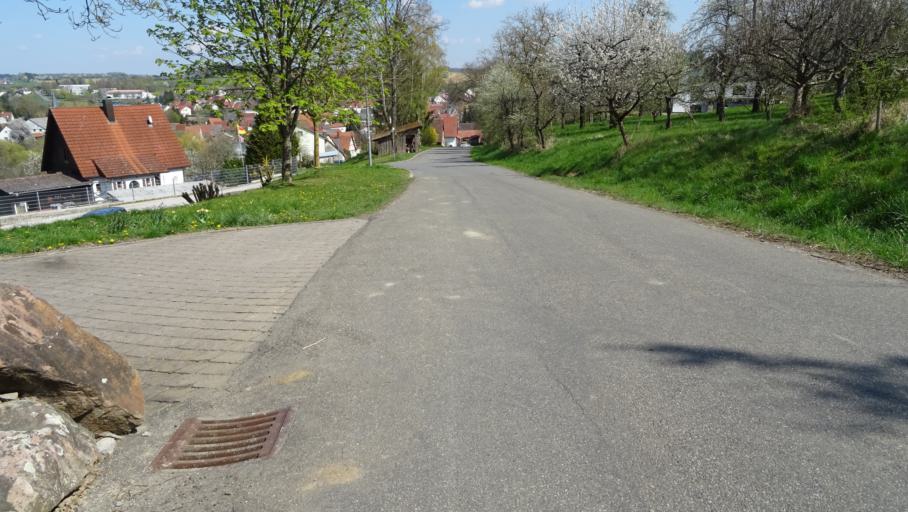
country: DE
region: Baden-Wuerttemberg
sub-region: Karlsruhe Region
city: Billigheim
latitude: 49.3905
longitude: 9.2626
